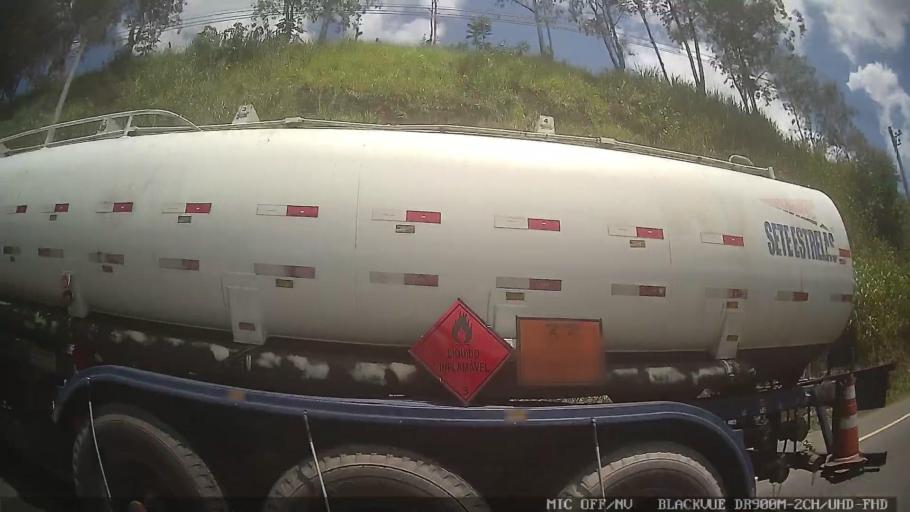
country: BR
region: Sao Paulo
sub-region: Santa Branca
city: Santa Branca
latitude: -23.3107
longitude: -45.7654
